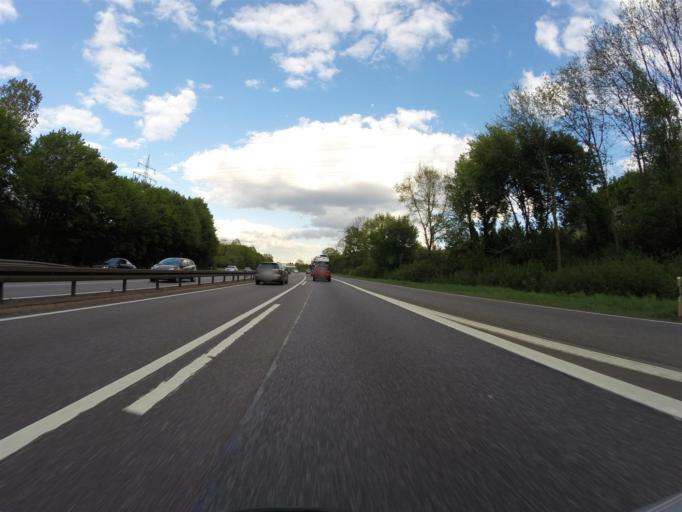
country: FR
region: Lorraine
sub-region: Departement de la Moselle
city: Schoeneck
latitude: 49.2439
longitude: 6.9129
